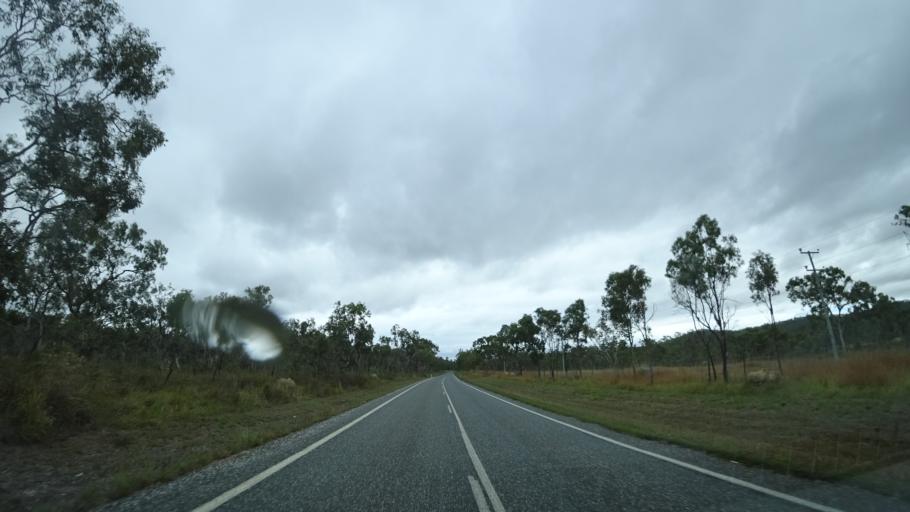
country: AU
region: Queensland
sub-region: Cairns
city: Port Douglas
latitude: -16.7226
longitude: 145.3531
